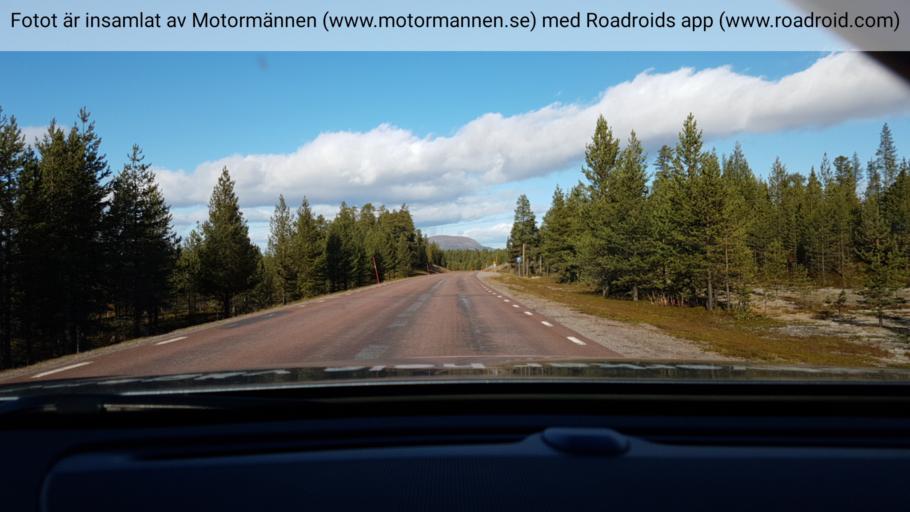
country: SE
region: Norrbotten
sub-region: Arjeplogs Kommun
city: Arjeplog
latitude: 66.0415
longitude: 18.0388
